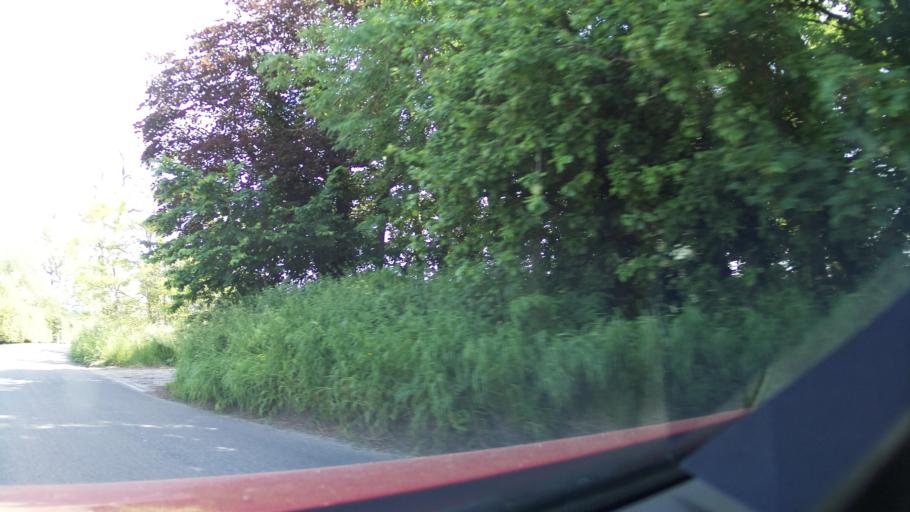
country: GB
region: England
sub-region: Wiltshire
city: Huish
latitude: 51.3530
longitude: -1.8033
